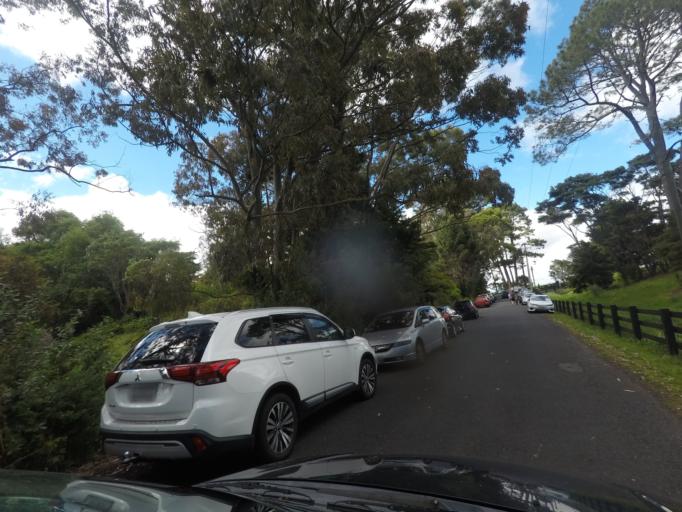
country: NZ
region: Auckland
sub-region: Auckland
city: Rothesay Bay
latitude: -36.7662
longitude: 174.6410
